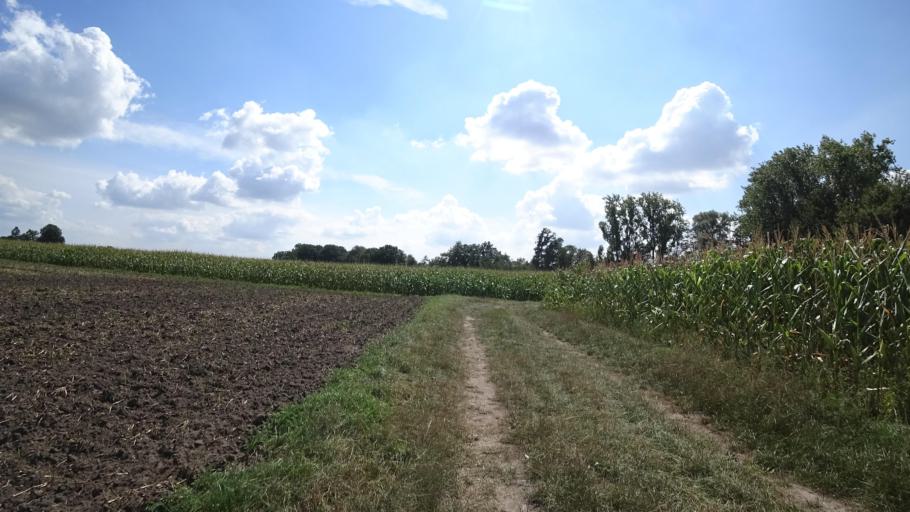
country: DE
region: North Rhine-Westphalia
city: Rietberg
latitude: 51.8671
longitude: 8.4401
